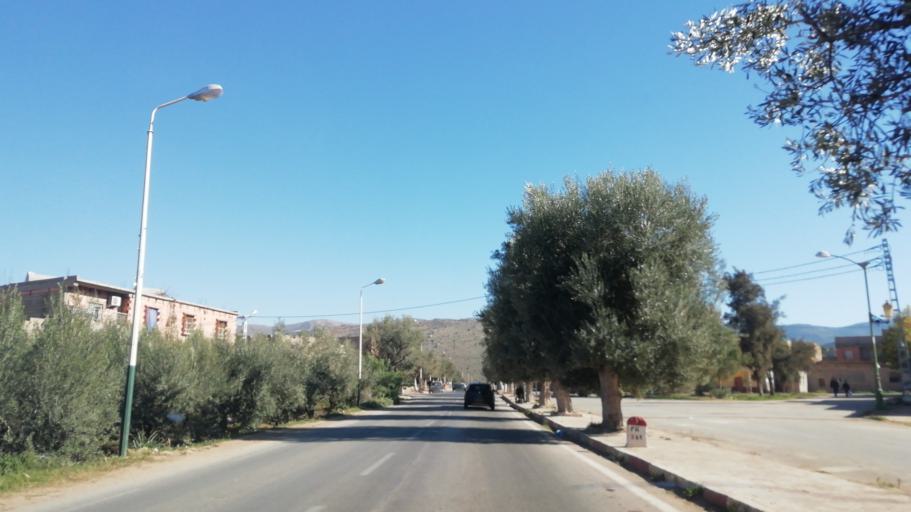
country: DZ
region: Tlemcen
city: Beni Mester
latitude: 34.8425
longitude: -1.4749
